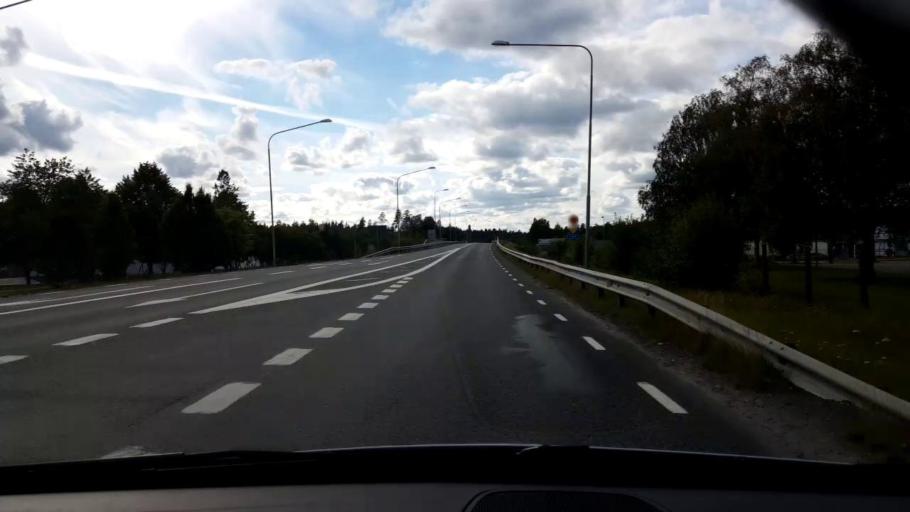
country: SE
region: Joenkoeping
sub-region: Savsjo Kommun
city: Saevsjoe
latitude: 57.3955
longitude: 14.6666
